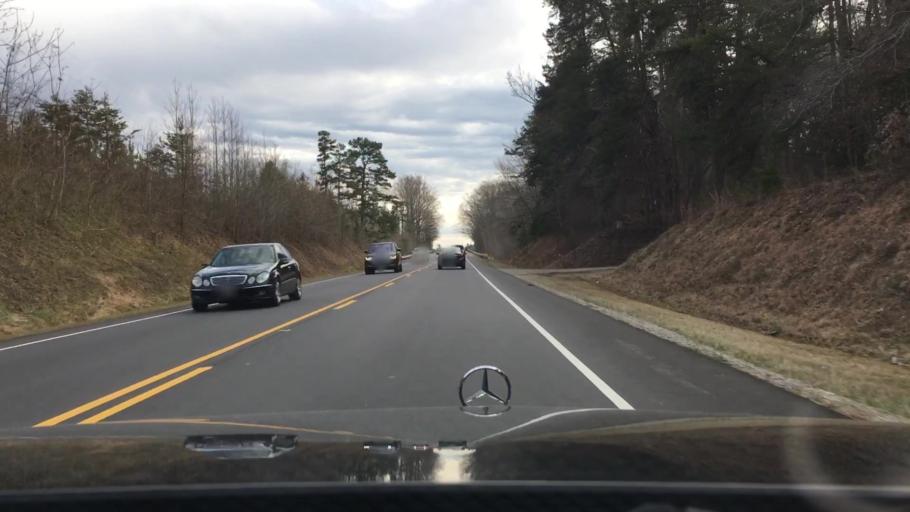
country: US
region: North Carolina
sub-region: Caswell County
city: Yanceyville
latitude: 36.4371
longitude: -79.3614
